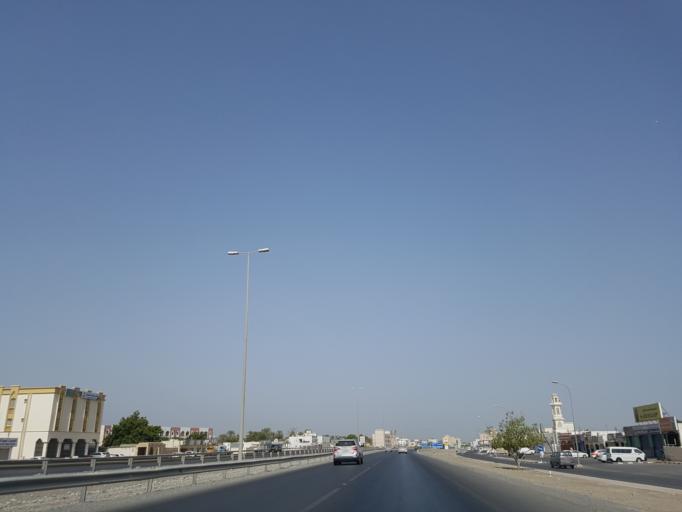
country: OM
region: Al Batinah
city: As Suwayq
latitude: 23.7438
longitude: 57.6254
